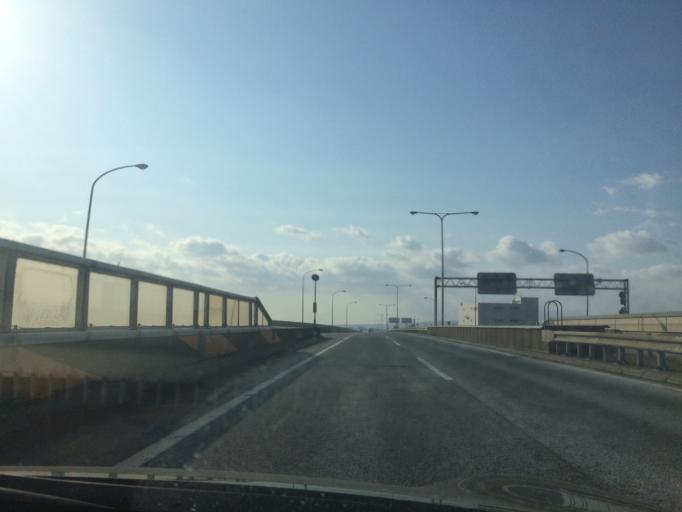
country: JP
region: Hokkaido
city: Sapporo
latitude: 43.0753
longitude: 141.4211
